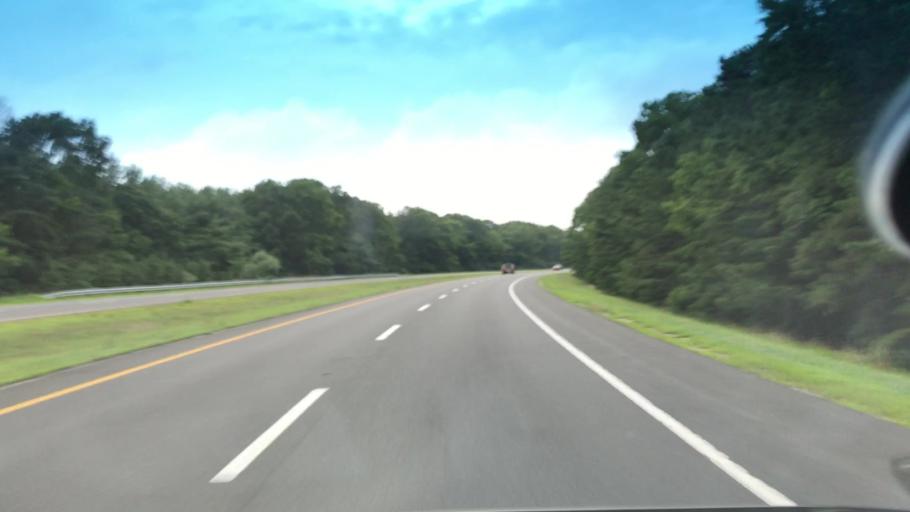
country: US
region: New York
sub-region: Suffolk County
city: Yaphank
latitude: 40.8546
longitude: -72.8995
